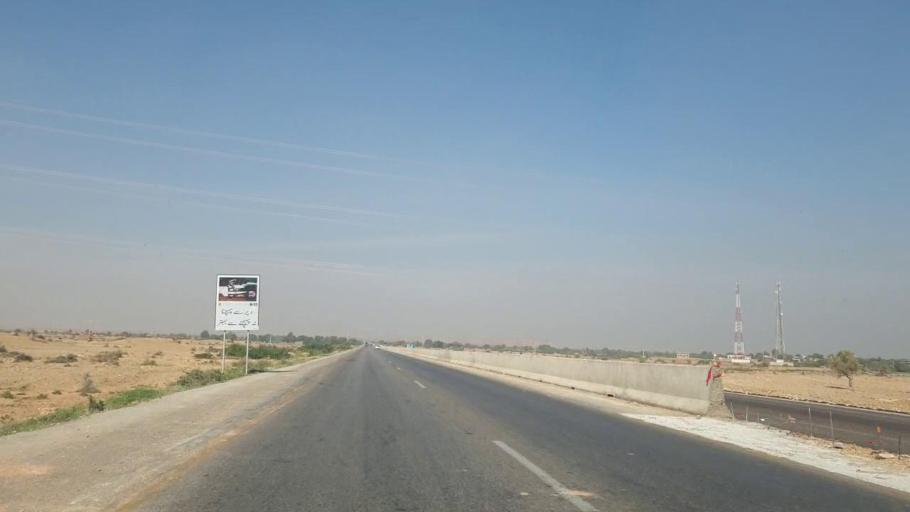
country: PK
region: Sindh
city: Matiari
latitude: 25.5871
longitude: 68.3107
